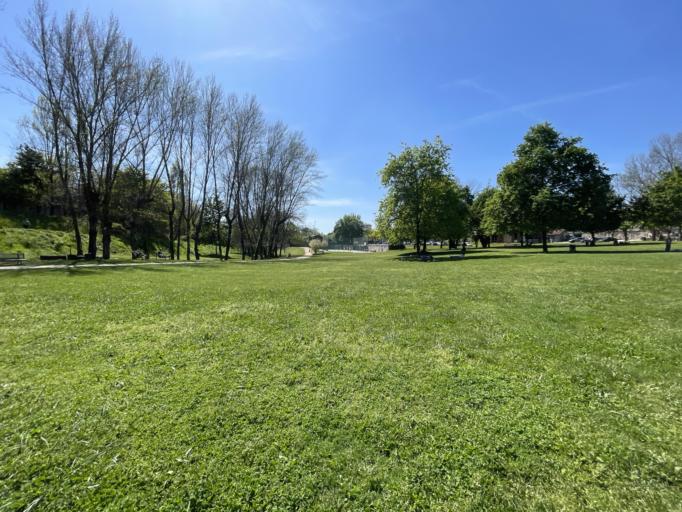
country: PT
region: Braga
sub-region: Guimaraes
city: Guimaraes
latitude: 41.4462
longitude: -8.2802
